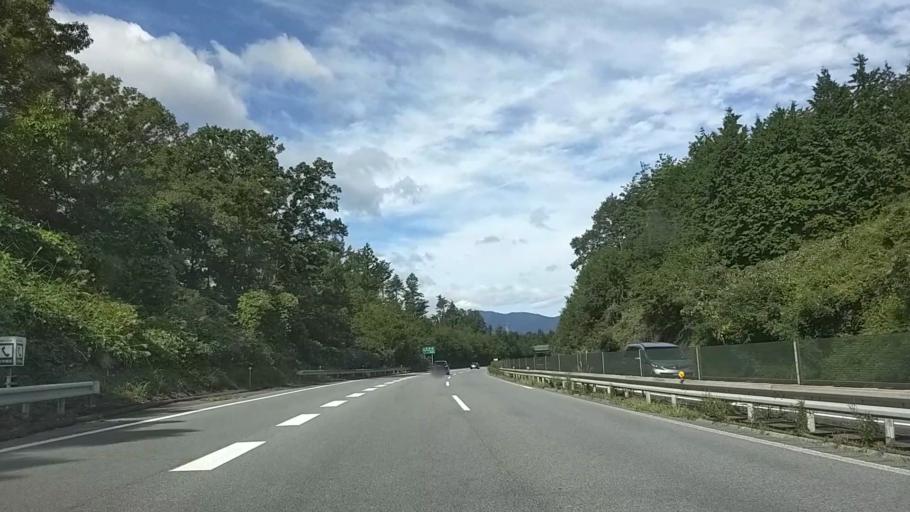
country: JP
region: Yamanashi
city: Nirasaki
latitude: 35.7922
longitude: 138.4034
